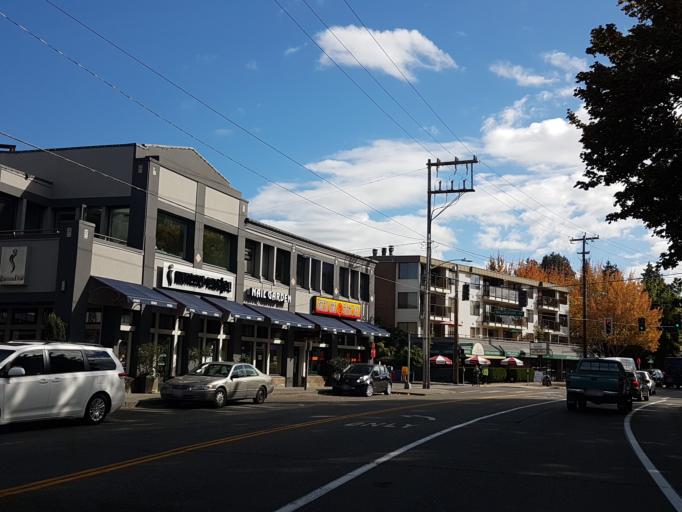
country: US
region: Washington
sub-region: King County
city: Shoreline
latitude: 47.6857
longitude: -122.3375
